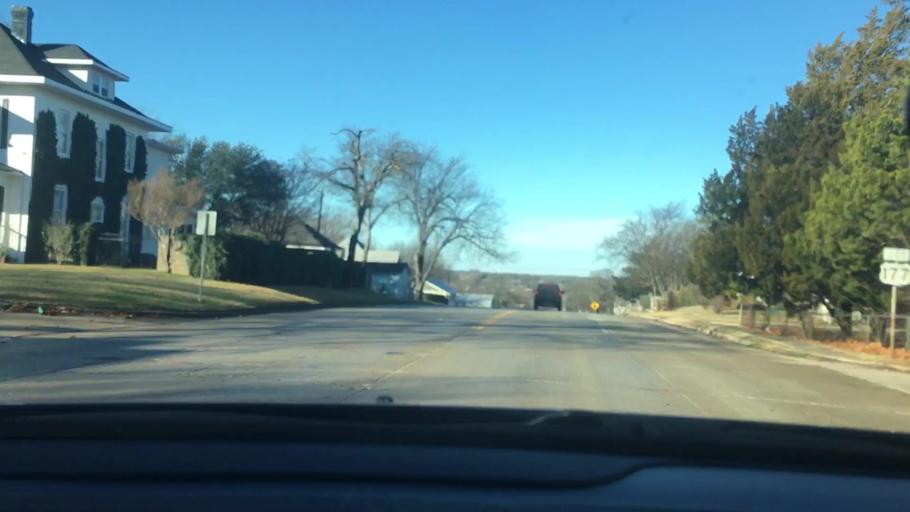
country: US
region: Oklahoma
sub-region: Murray County
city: Sulphur
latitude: 34.5110
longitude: -96.9647
